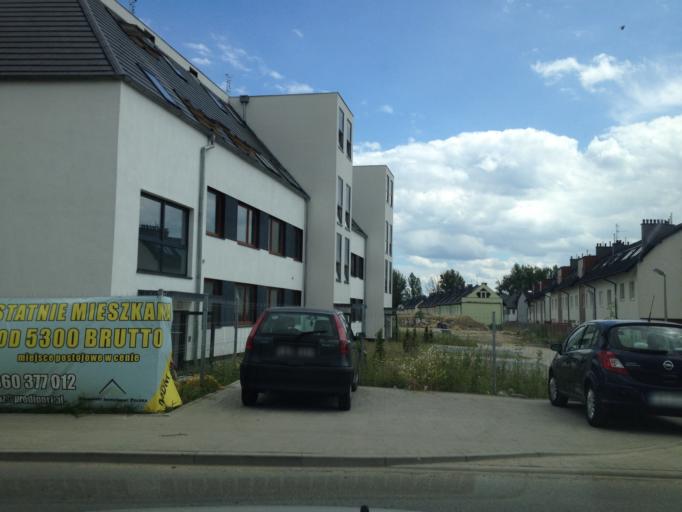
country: PL
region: Lower Silesian Voivodeship
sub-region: Powiat wroclawski
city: Smolec
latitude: 51.0953
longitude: 16.9346
